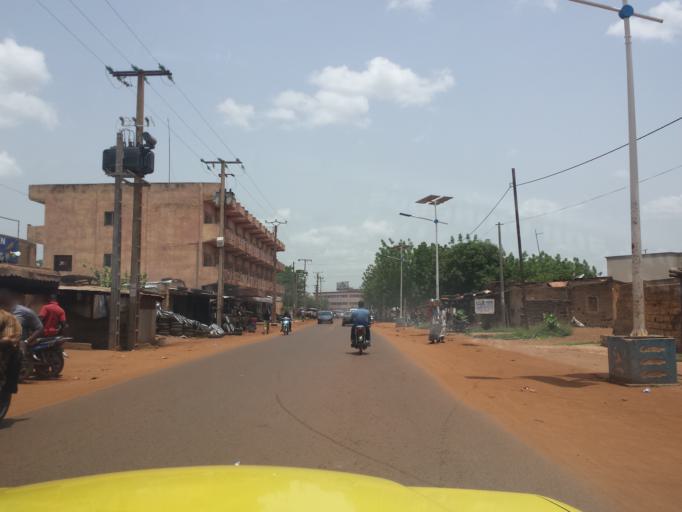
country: ML
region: Bamako
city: Bamako
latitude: 12.6030
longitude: -7.9635
